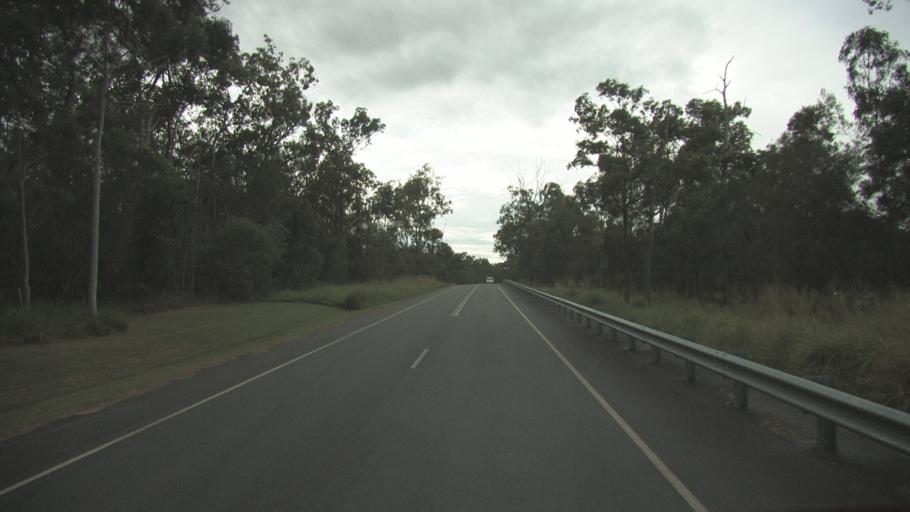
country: AU
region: Queensland
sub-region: Logan
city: Park Ridge South
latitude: -27.7433
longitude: 153.0257
